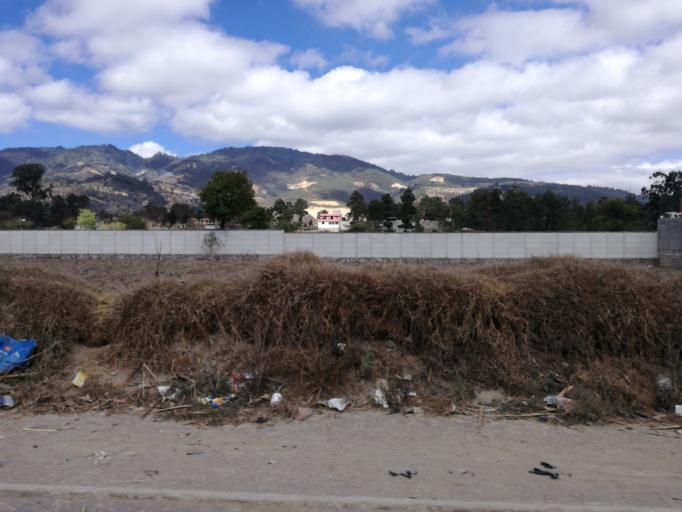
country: GT
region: Quetzaltenango
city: Quetzaltenango
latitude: 14.8129
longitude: -91.5390
